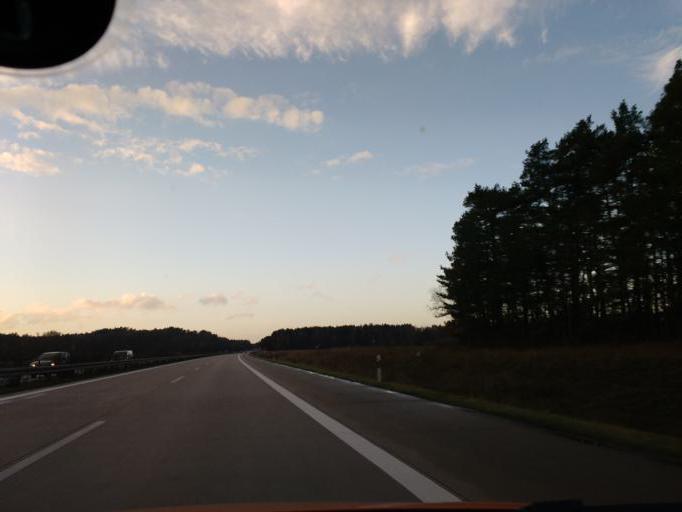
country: DE
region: Mecklenburg-Vorpommern
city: Rastow
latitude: 53.4413
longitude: 11.3798
